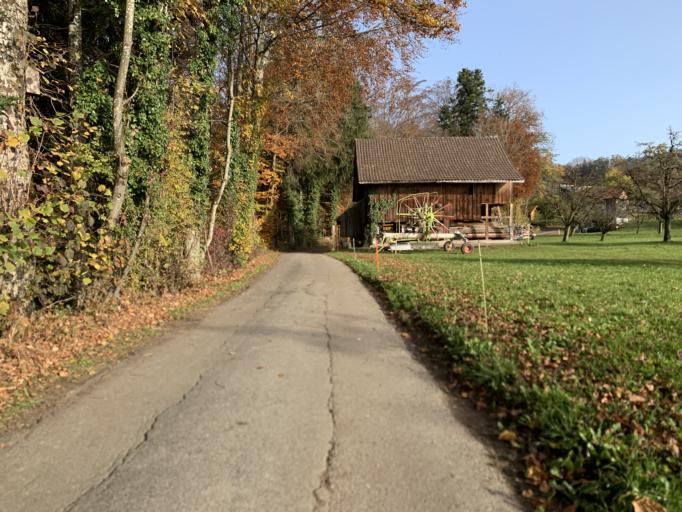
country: CH
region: Zurich
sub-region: Bezirk Hinwil
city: Hinwil
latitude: 47.2989
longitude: 8.8529
